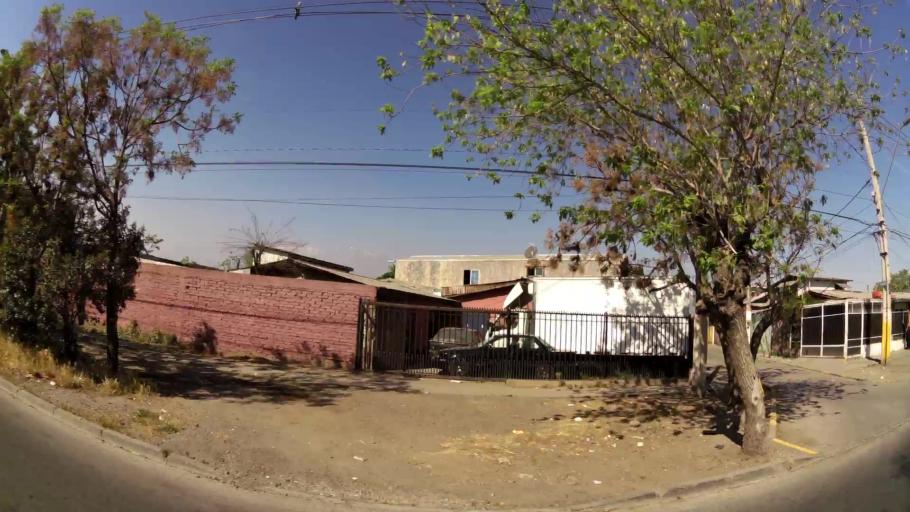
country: CL
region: Santiago Metropolitan
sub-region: Provincia de Santiago
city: La Pintana
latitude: -33.5302
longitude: -70.6098
